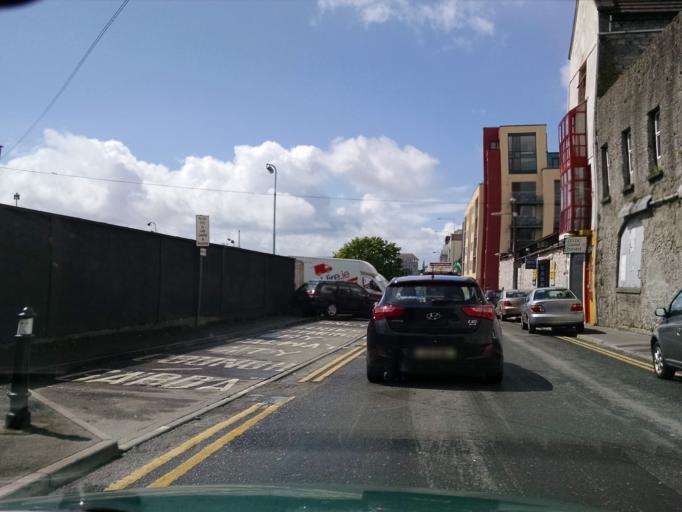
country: IE
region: Connaught
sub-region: County Galway
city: Gaillimh
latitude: 53.2729
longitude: -9.0481
